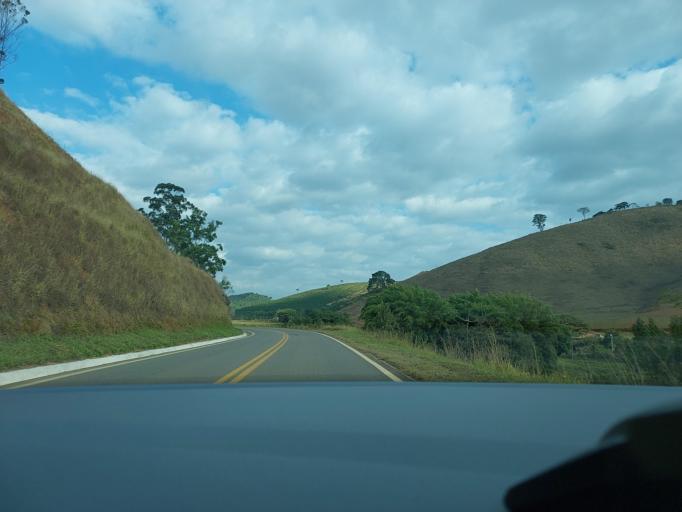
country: BR
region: Minas Gerais
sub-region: Visconde Do Rio Branco
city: Visconde do Rio Branco
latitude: -20.8751
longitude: -42.6689
